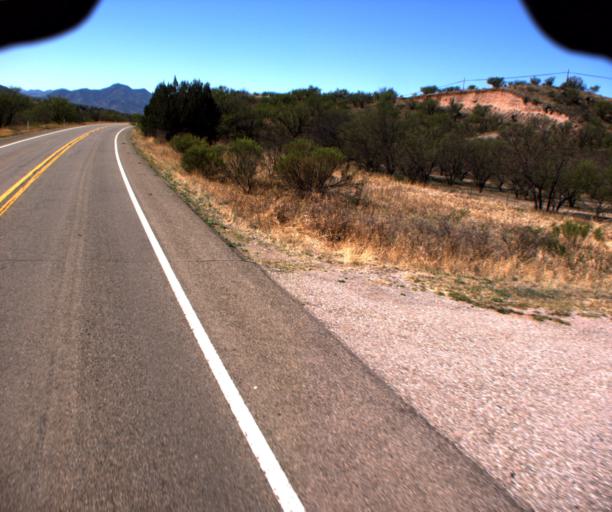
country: US
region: Arizona
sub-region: Santa Cruz County
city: Rio Rico
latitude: 31.6350
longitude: -110.7133
